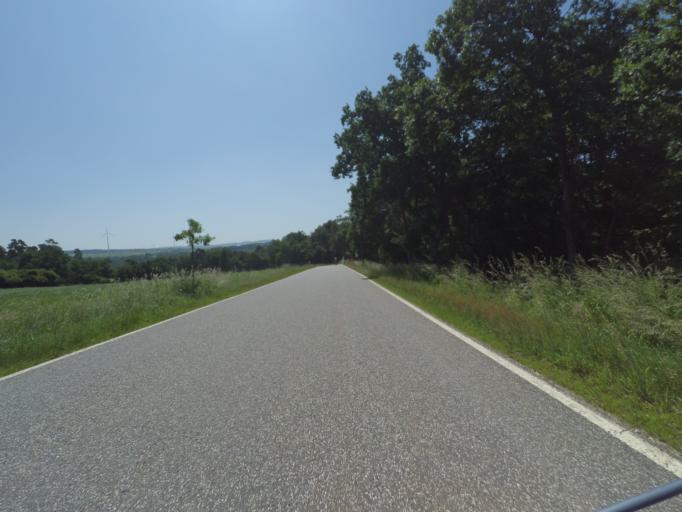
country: DE
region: Rheinland-Pfalz
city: Lahr
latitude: 50.1173
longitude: 7.3627
